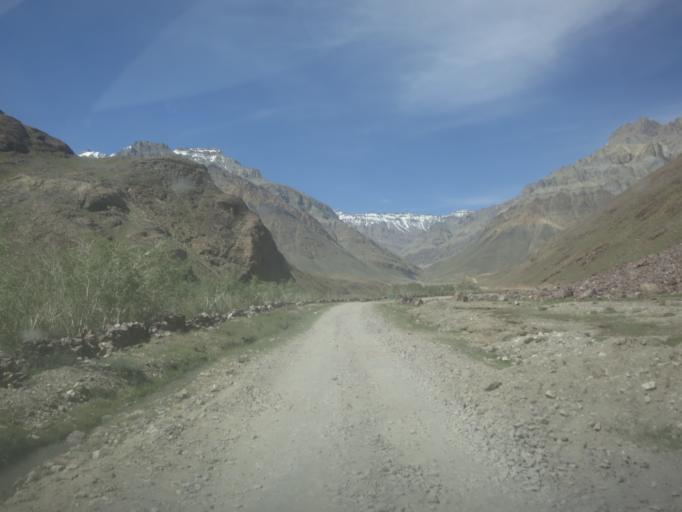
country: IN
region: Himachal Pradesh
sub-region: Kulu
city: Manali
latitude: 32.4420
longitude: 77.6864
